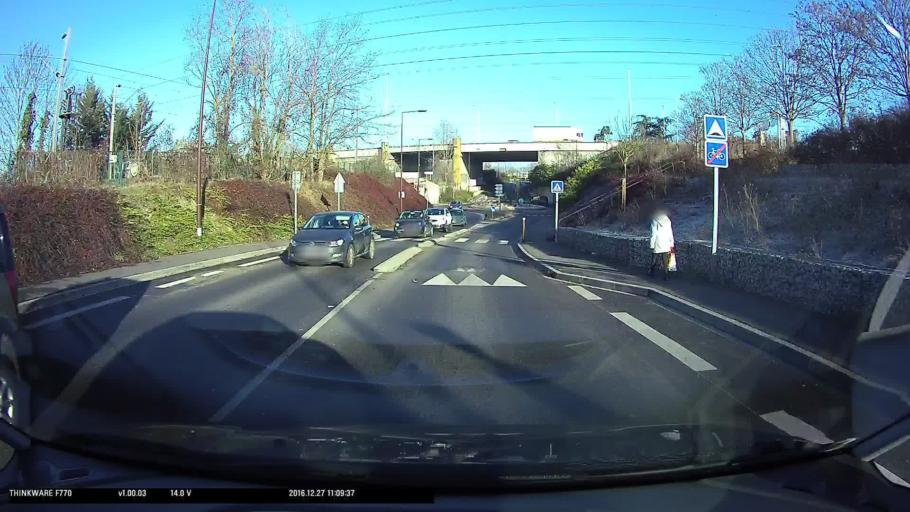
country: FR
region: Ile-de-France
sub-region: Departement du Val-d'Oise
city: Eragny
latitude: 49.0331
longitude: 2.1019
